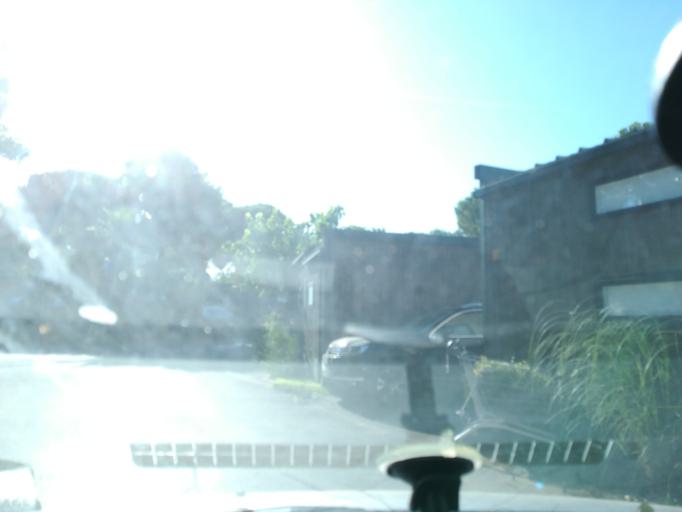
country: FR
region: Languedoc-Roussillon
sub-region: Departement de l'Herault
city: Portiragnes
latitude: 43.2818
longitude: 3.3637
